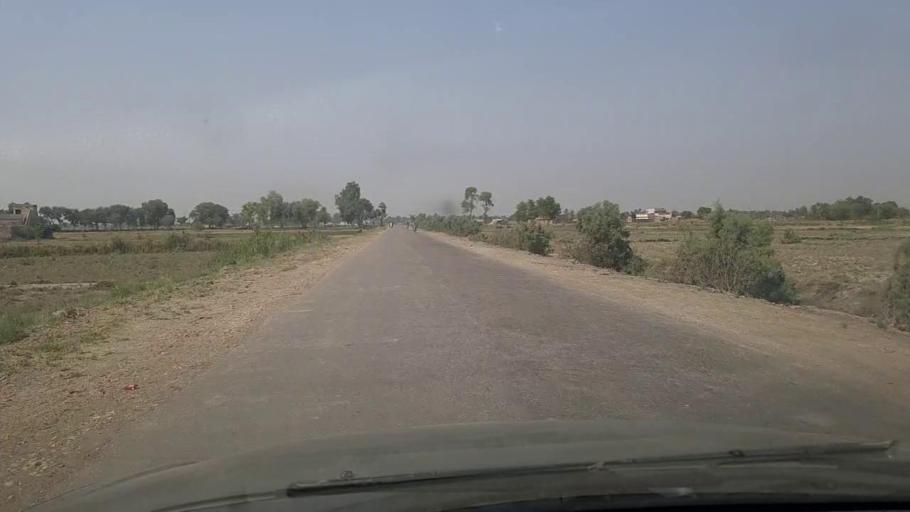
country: PK
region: Sindh
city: Khanpur
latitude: 27.8990
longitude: 69.4945
